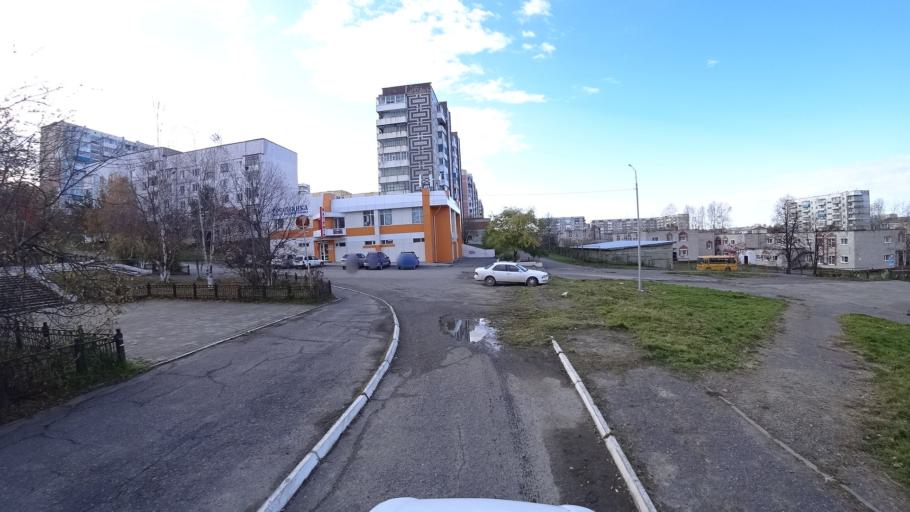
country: RU
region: Khabarovsk Krai
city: Amursk
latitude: 50.2465
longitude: 136.9195
